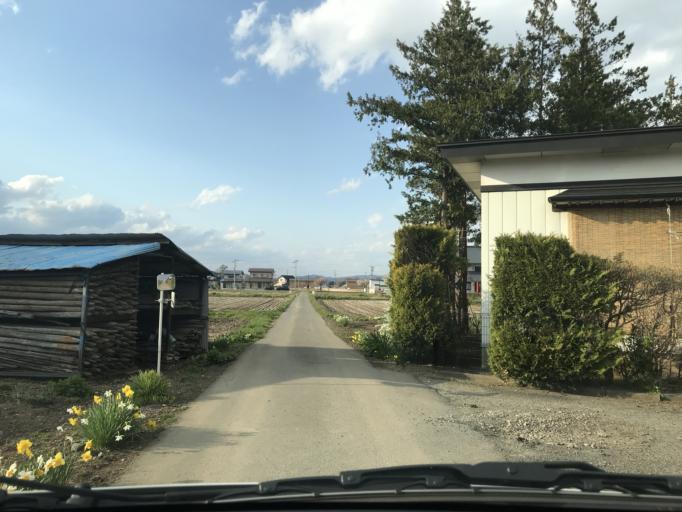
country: JP
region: Iwate
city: Mizusawa
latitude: 39.1749
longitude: 141.1347
